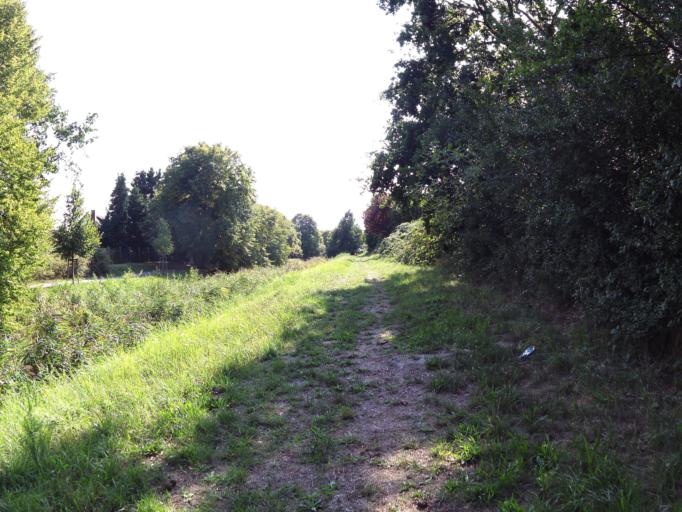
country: DE
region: Mecklenburg-Vorpommern
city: Seebad Bansin
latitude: 53.9622
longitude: 14.1497
